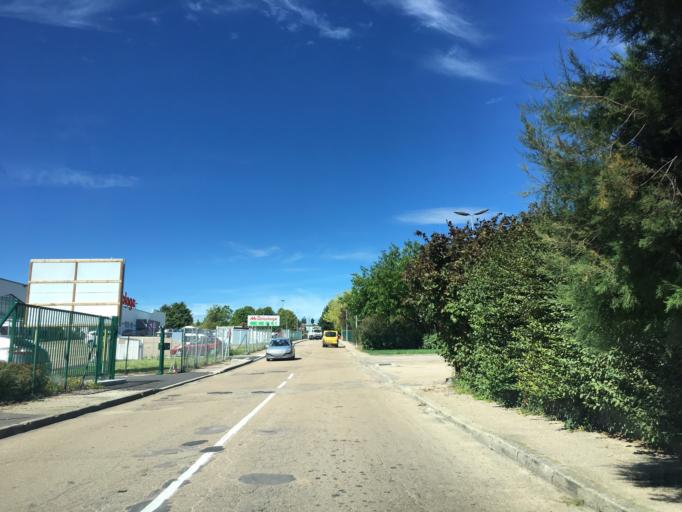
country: FR
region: Bourgogne
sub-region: Departement de l'Yonne
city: Auxerre
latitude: 47.8175
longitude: 3.5765
